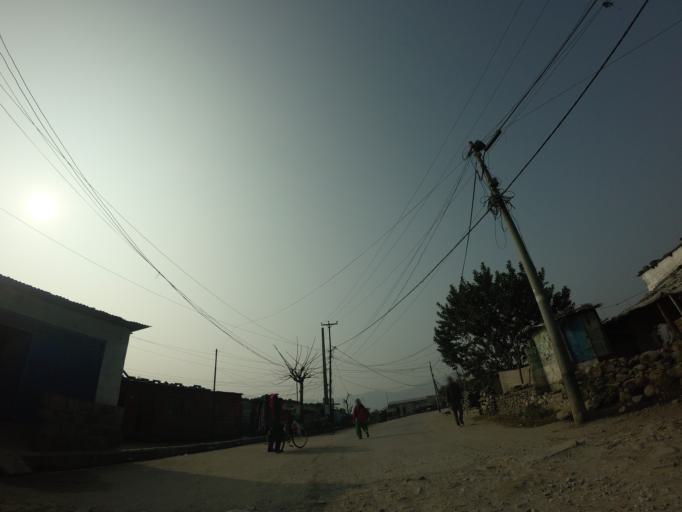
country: NP
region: Western Region
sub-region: Gandaki Zone
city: Pokhara
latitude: 28.2074
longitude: 83.9891
